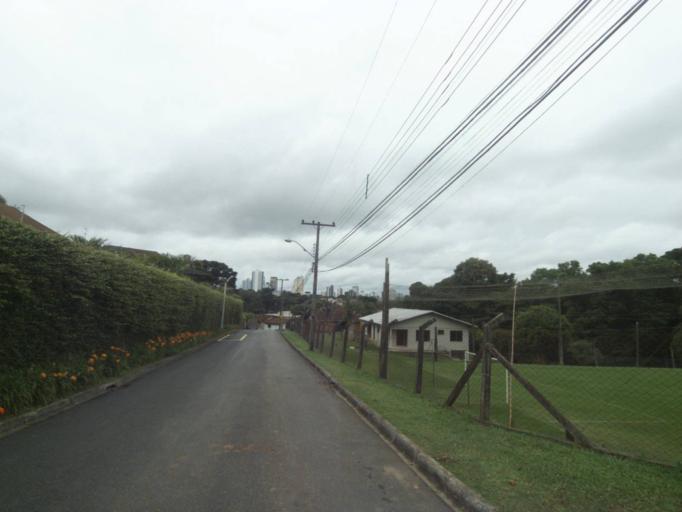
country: BR
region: Parana
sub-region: Curitiba
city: Curitiba
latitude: -25.4509
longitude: -49.3349
